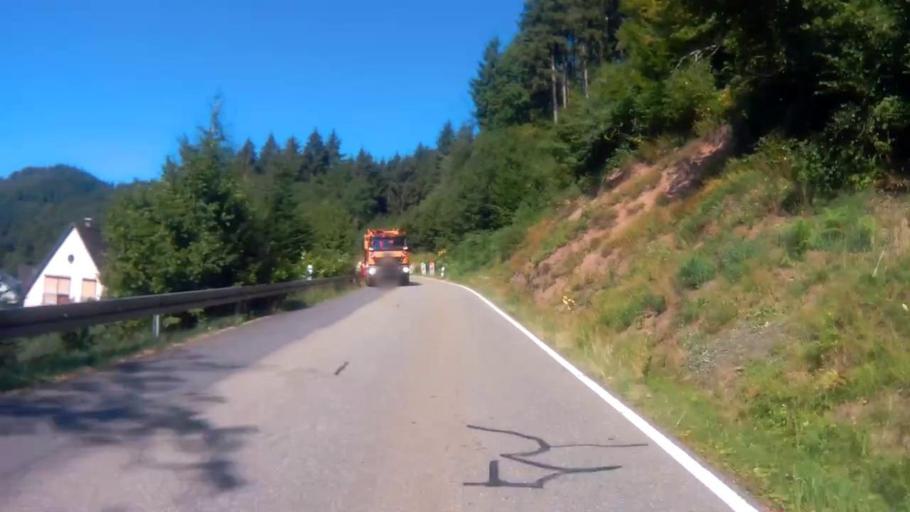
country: DE
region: Baden-Wuerttemberg
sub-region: Freiburg Region
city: Hausen
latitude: 47.6827
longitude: 7.8360
